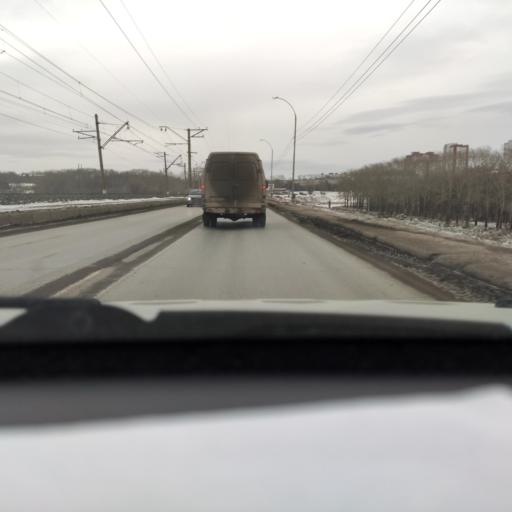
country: RU
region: Perm
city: Perm
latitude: 58.1147
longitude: 56.3570
